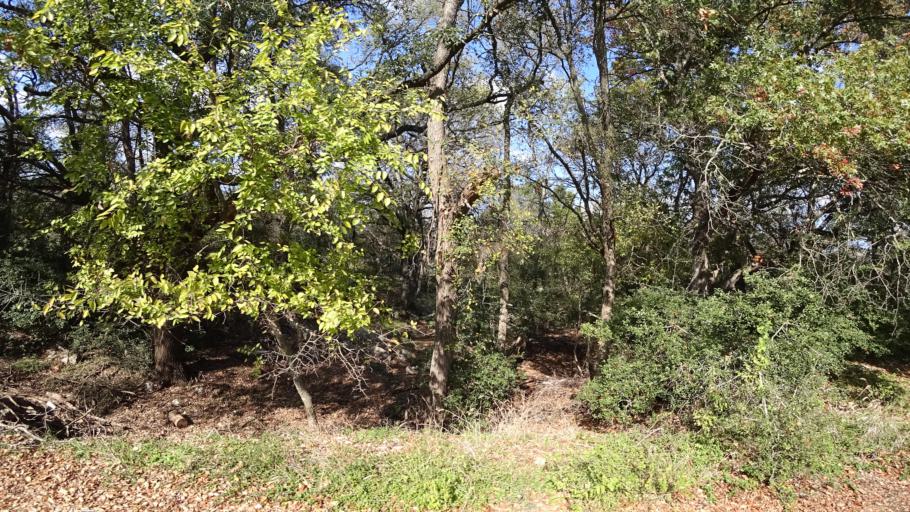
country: US
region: Texas
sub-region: Travis County
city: Shady Hollow
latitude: 30.1788
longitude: -97.8490
